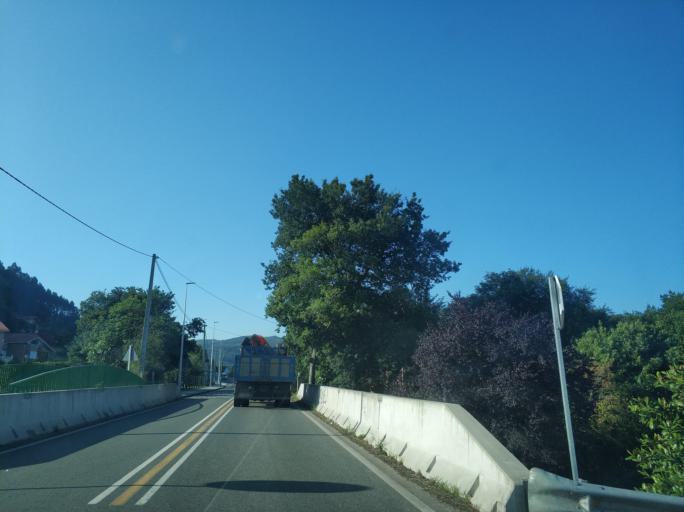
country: ES
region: Cantabria
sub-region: Provincia de Cantabria
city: Polanco
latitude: 43.3665
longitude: -3.9581
